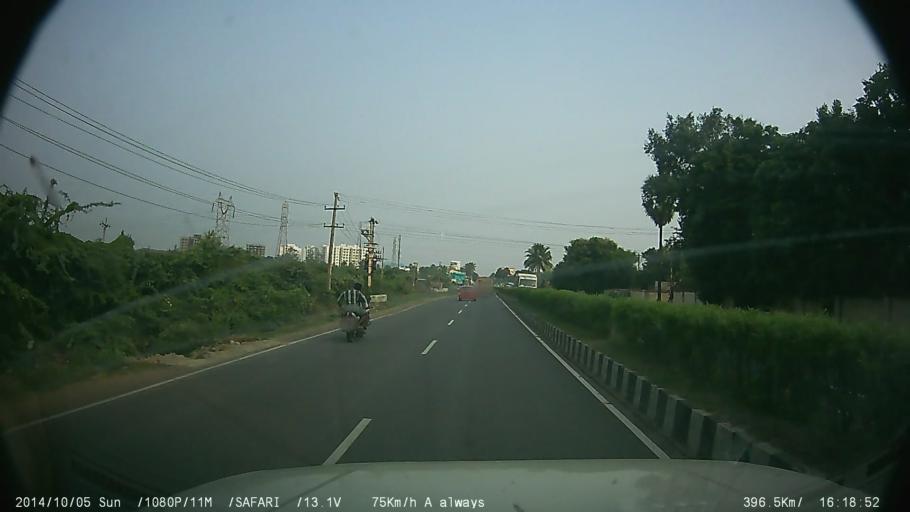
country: IN
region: Tamil Nadu
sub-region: Kancheepuram
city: Vengavasal
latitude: 12.8554
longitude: 80.1363
